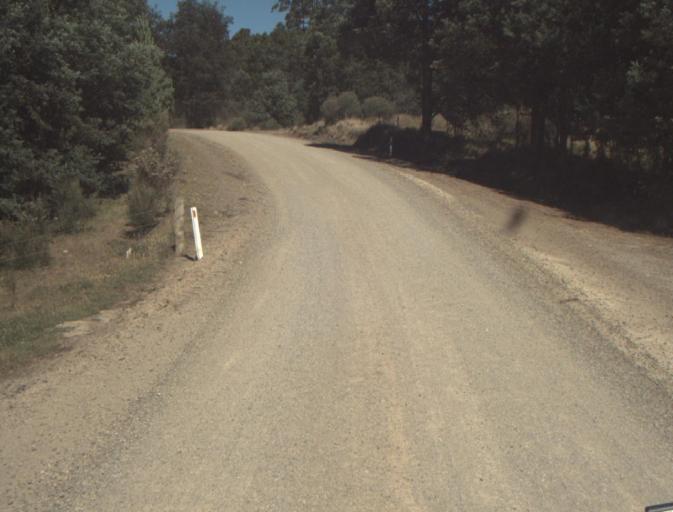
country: AU
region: Tasmania
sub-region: Dorset
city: Scottsdale
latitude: -41.3601
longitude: 147.4608
